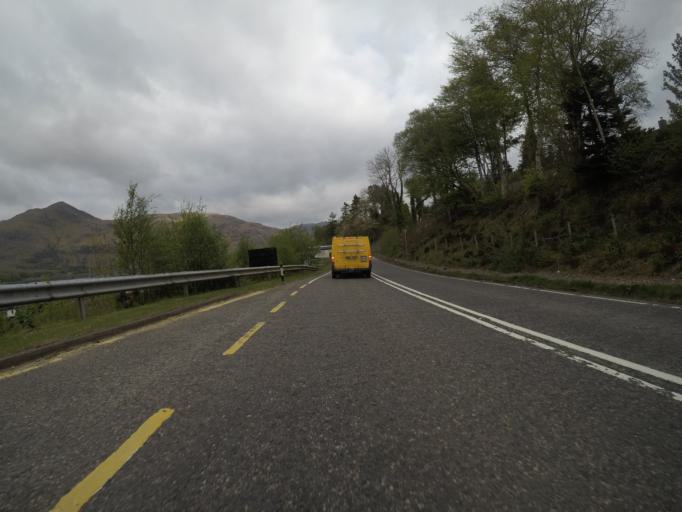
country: GB
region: Scotland
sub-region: Highland
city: Fort William
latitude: 56.7215
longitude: -5.2323
